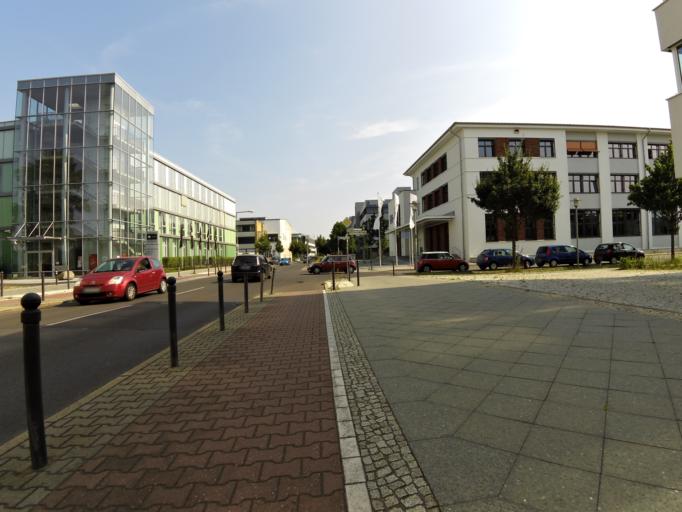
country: DE
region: Berlin
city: Adlershof
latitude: 52.4305
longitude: 13.5403
